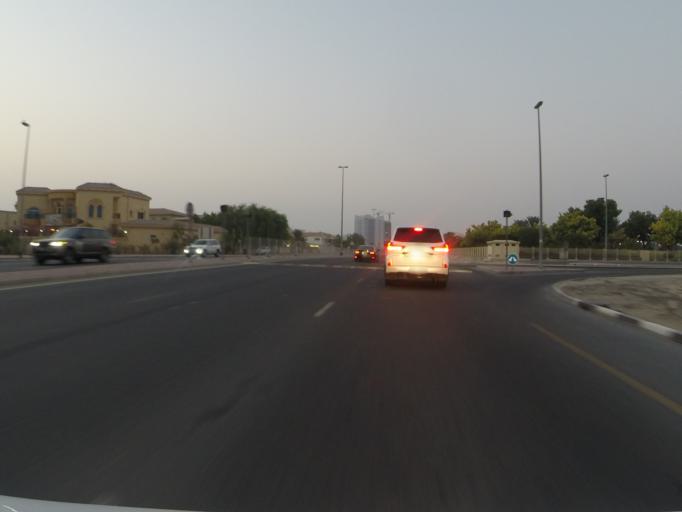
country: AE
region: Dubai
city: Dubai
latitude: 25.0995
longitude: 55.1998
